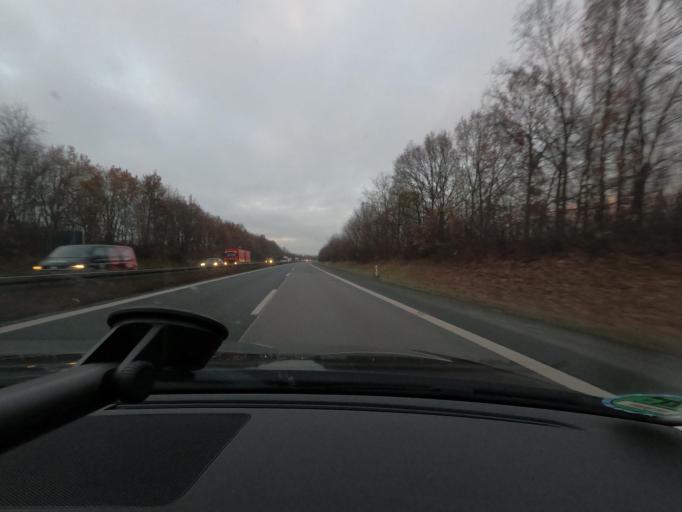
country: DE
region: Bavaria
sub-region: Upper Franconia
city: Altendorf
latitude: 49.8032
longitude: 11.0175
